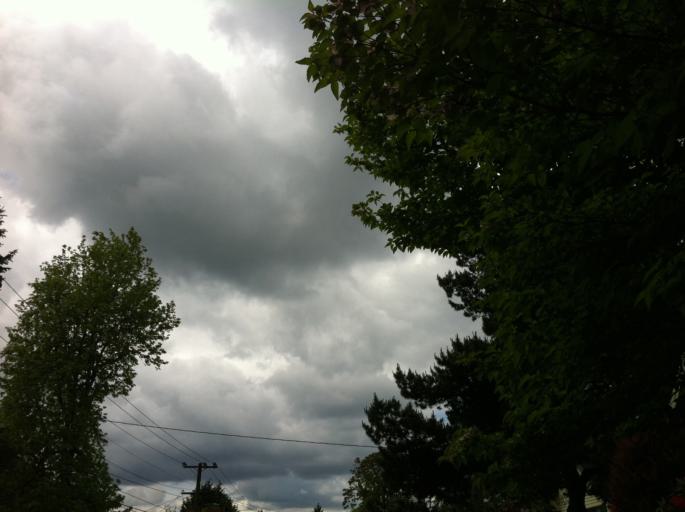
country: US
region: Oregon
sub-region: Clackamas County
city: Lake Oswego
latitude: 45.4642
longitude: -122.6906
